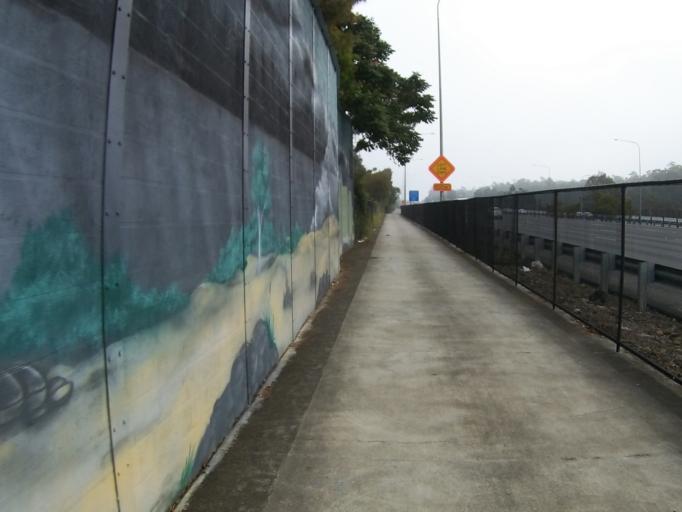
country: AU
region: Queensland
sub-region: Brisbane
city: Nathan
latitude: -27.5534
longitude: 153.0691
